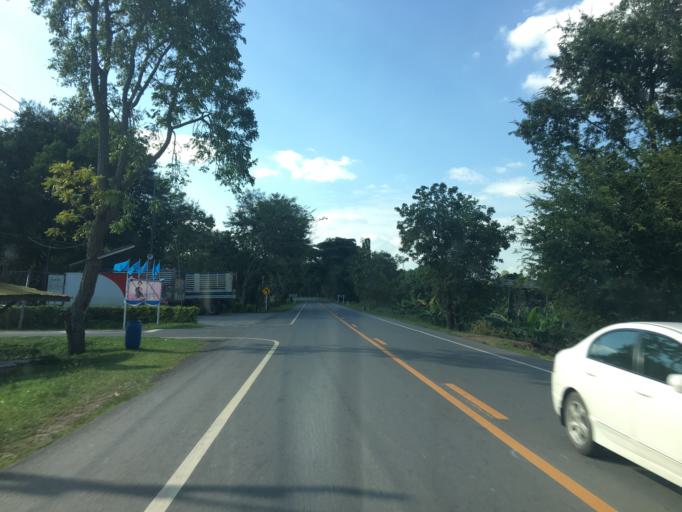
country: TH
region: Phayao
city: Chun
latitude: 19.3478
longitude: 100.1137
